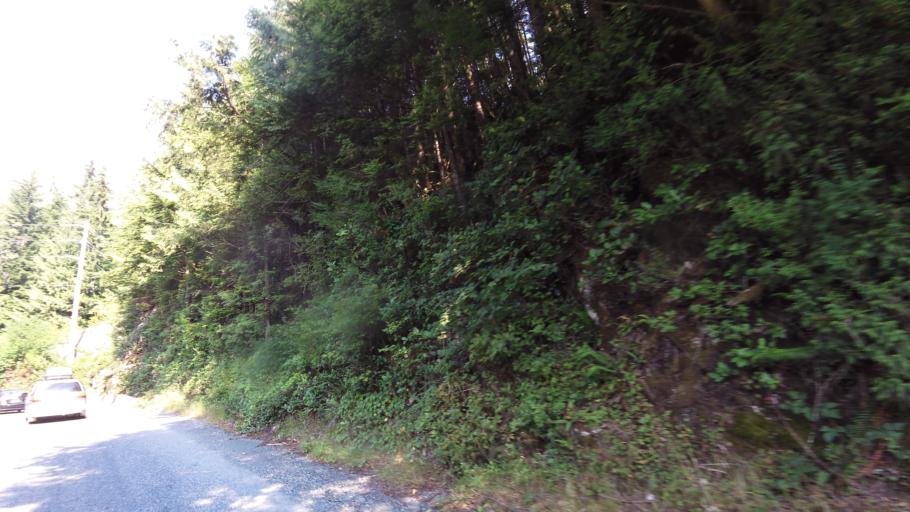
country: CA
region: British Columbia
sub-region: Regional District of Alberni-Clayoquot
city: Ucluelet
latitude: 49.0901
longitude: -125.4536
